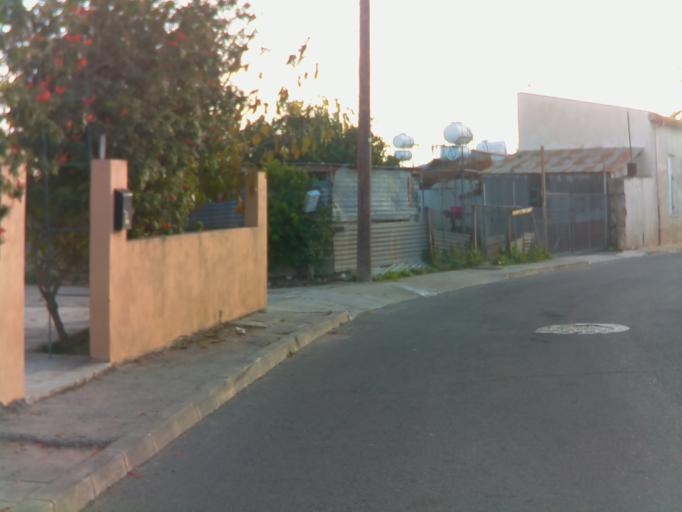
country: CY
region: Pafos
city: Paphos
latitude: 34.7826
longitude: 32.4183
